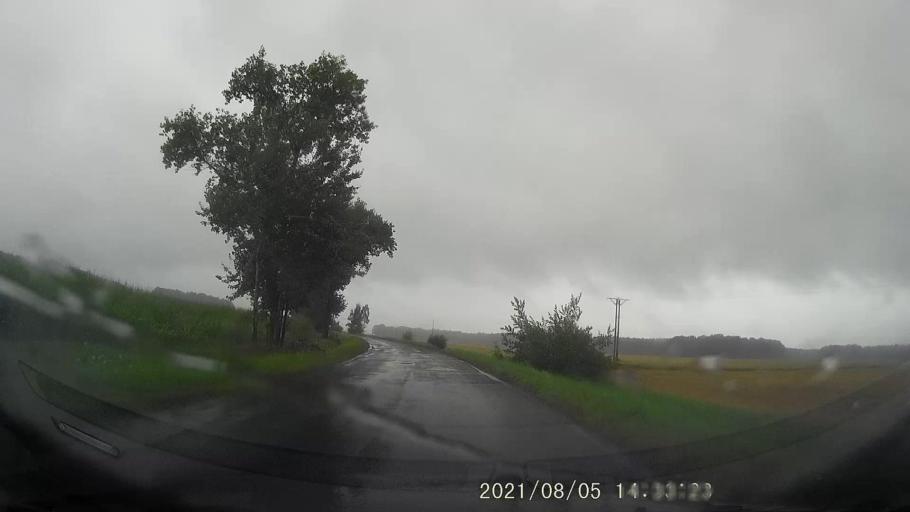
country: PL
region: Opole Voivodeship
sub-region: Powiat nyski
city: Korfantow
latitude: 50.4685
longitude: 17.5388
